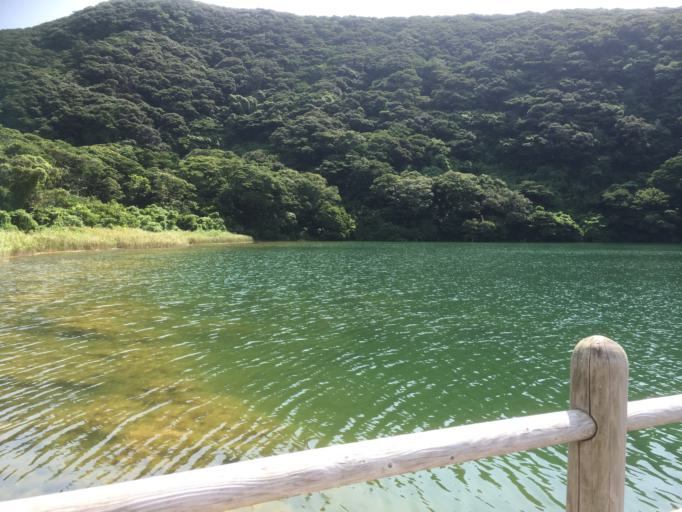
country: JP
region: Shizuoka
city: Shimoda
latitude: 34.0557
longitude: 139.5261
